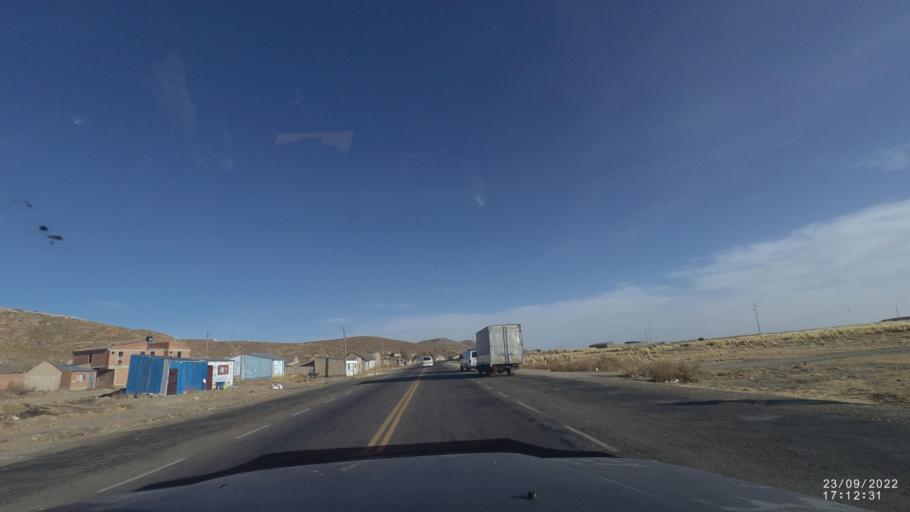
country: BO
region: Oruro
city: Totoral
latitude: -18.7048
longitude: -66.8768
